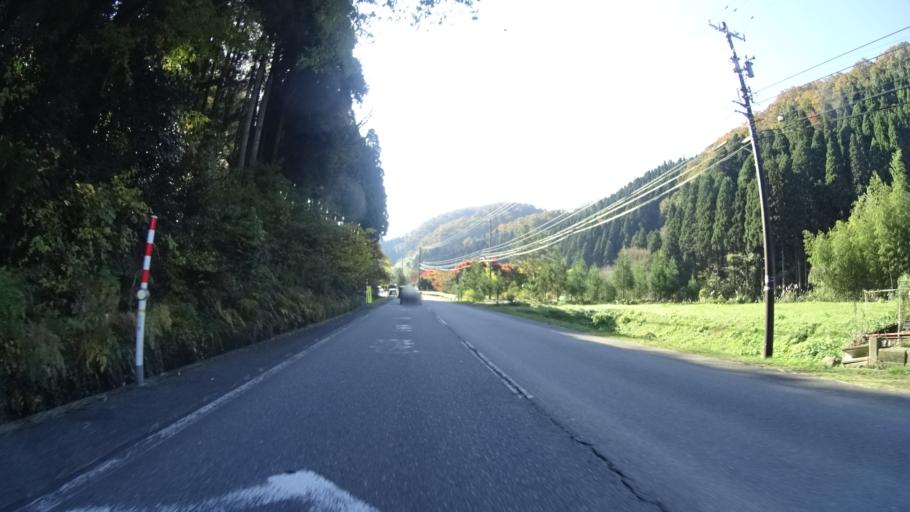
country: JP
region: Ishikawa
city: Komatsu
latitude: 36.3762
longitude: 136.5422
